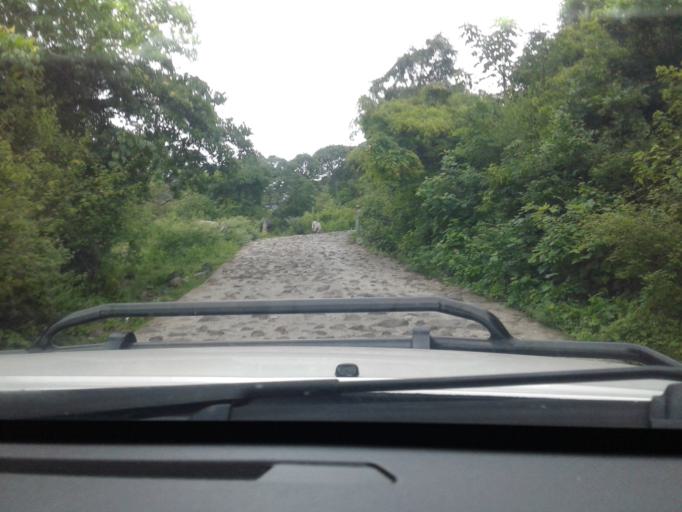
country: NI
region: Leon
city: Santa Rosa del Penon
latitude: 12.9009
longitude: -86.2283
